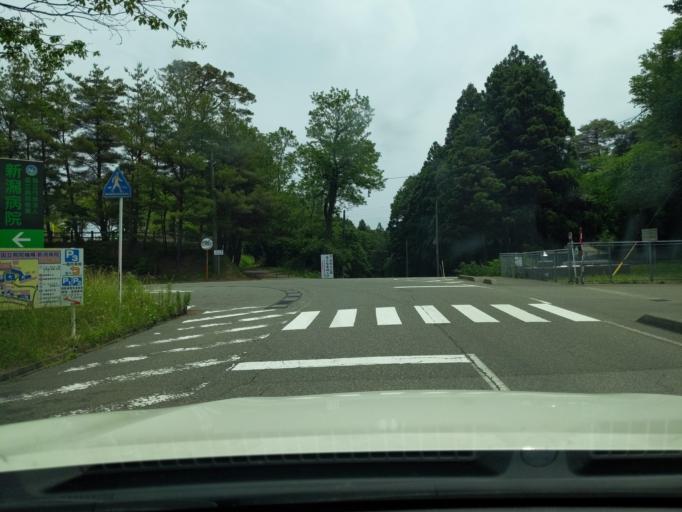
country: JP
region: Niigata
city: Kashiwazaki
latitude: 37.3576
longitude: 138.5388
